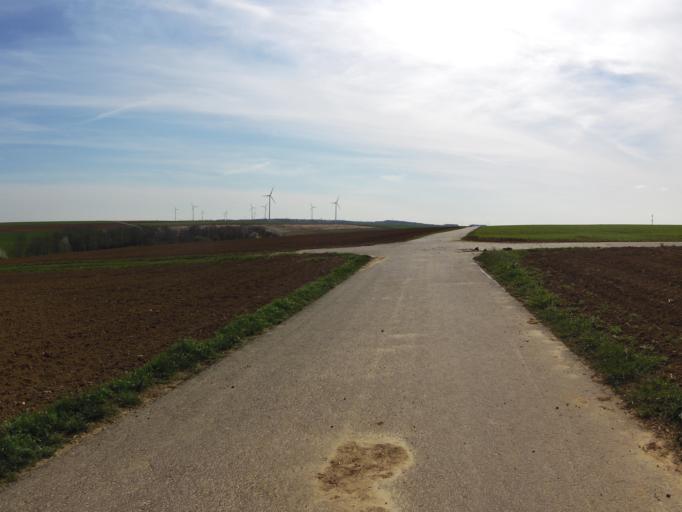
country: DE
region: Bavaria
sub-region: Regierungsbezirk Unterfranken
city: Mainstockheim
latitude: 49.7966
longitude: 10.1408
